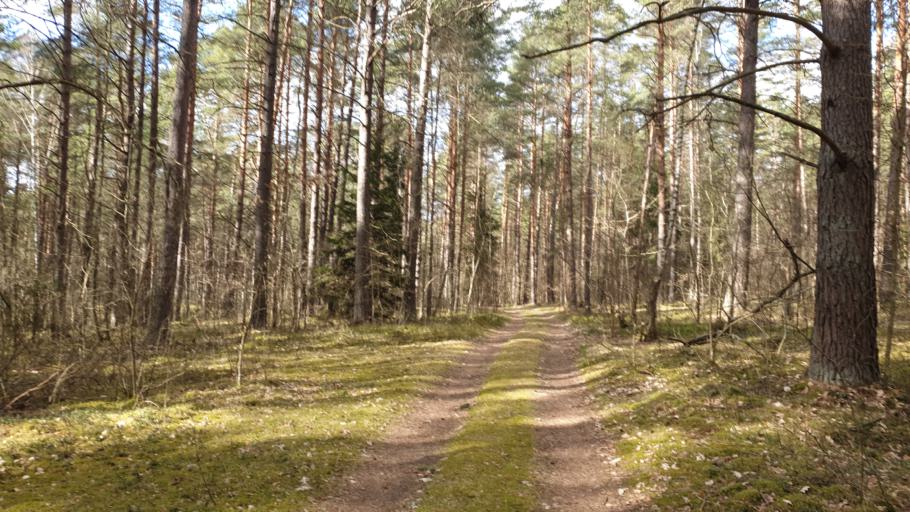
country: LT
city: Grigiskes
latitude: 54.7281
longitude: 25.0320
